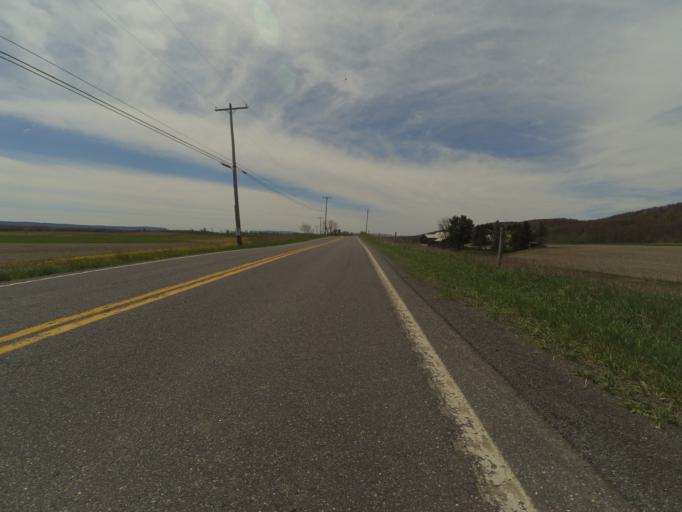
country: US
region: Pennsylvania
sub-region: Centre County
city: Stormstown
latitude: 40.7429
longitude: -78.0859
